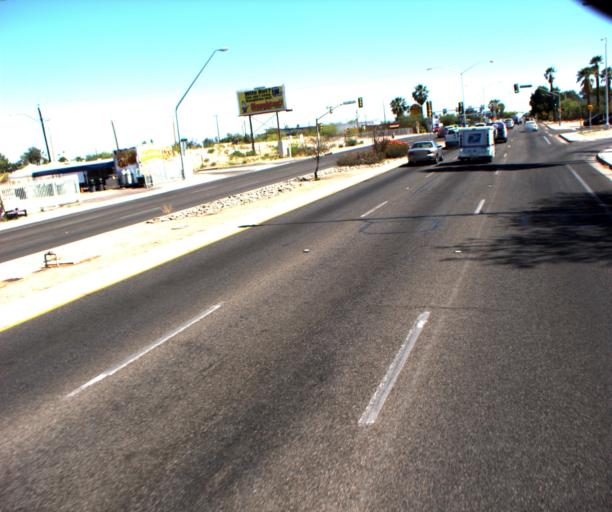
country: US
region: Arizona
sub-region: Pima County
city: Flowing Wells
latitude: 32.2618
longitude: -110.9782
